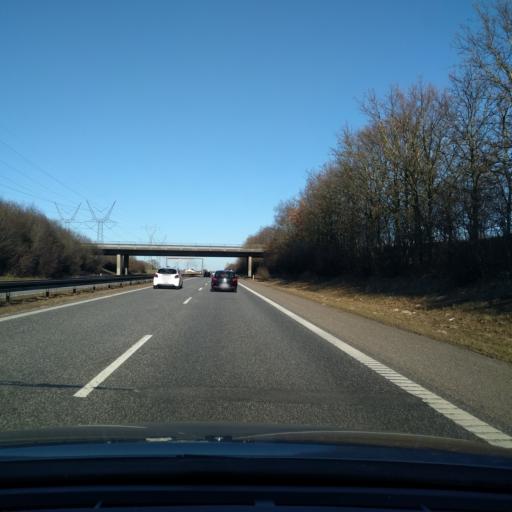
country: DK
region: South Denmark
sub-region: Odense Kommune
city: Neder Holluf
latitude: 55.3555
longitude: 10.4779
